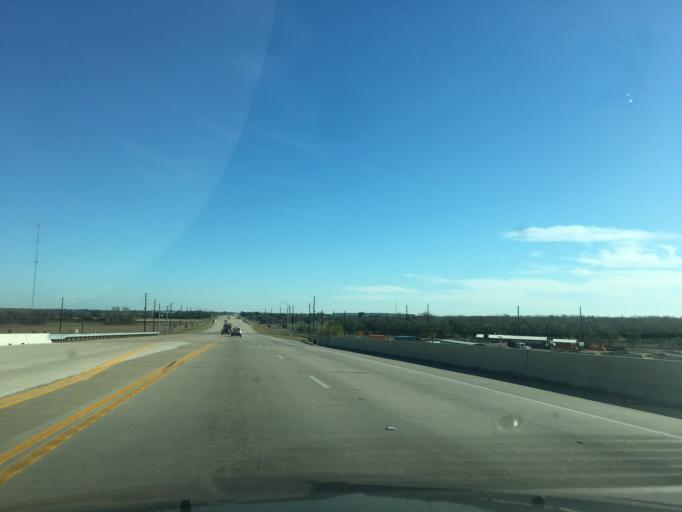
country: US
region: Texas
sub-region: Fort Bend County
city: Rosenberg
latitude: 29.5238
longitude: -95.8741
